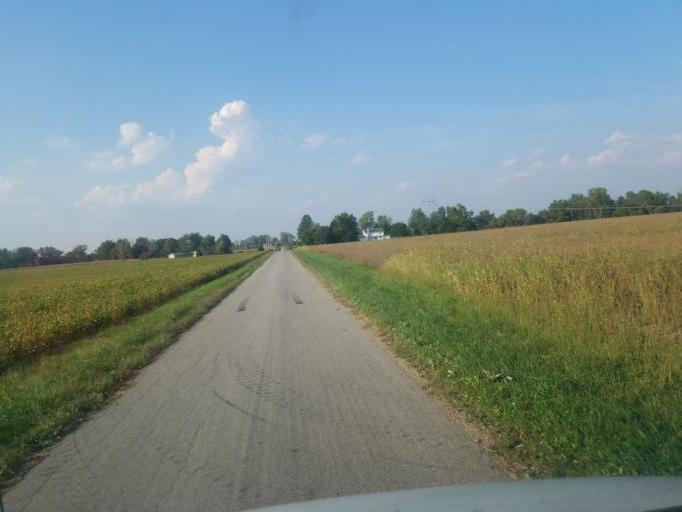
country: US
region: Ohio
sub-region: Wyandot County
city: Upper Sandusky
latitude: 40.9281
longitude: -83.1893
